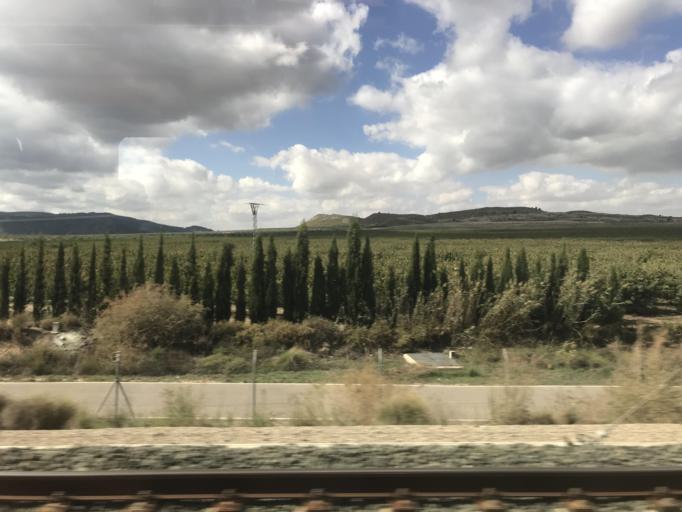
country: ES
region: Valencia
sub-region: Provincia de Alicante
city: Villena
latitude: 38.5907
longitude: -0.8758
